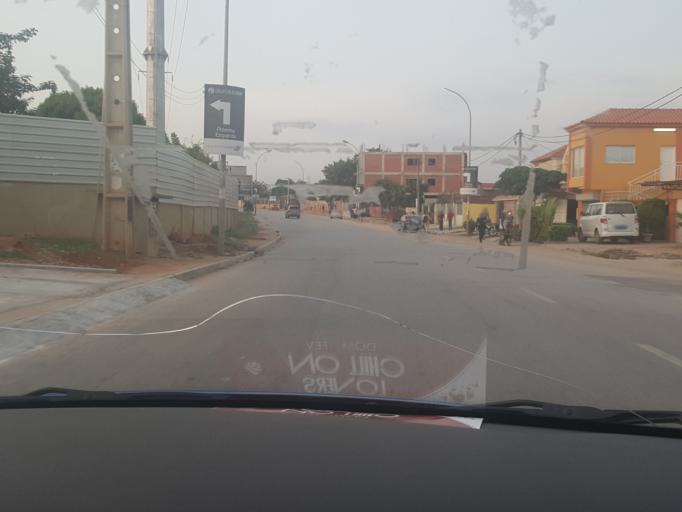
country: AO
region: Luanda
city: Luanda
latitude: -8.9136
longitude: 13.2018
